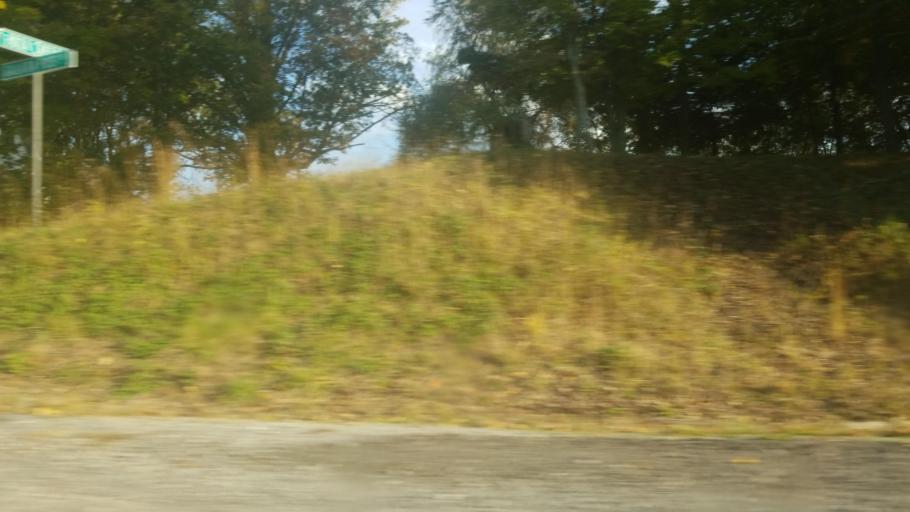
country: US
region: Illinois
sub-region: Williamson County
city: Marion
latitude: 37.7621
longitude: -88.7808
